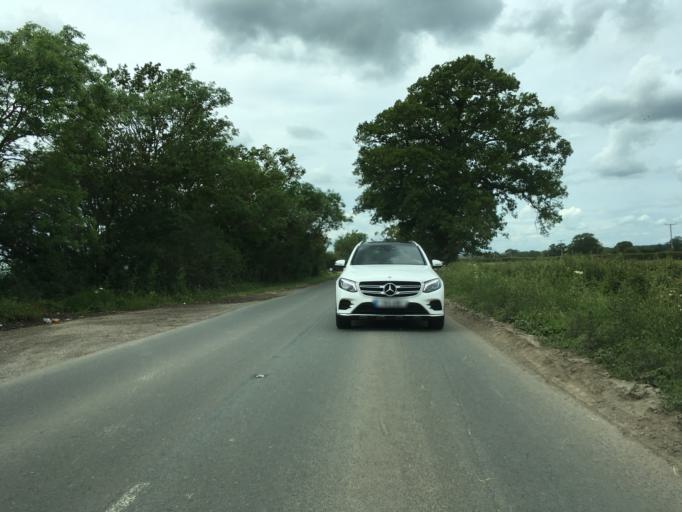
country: GB
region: England
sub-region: Wiltshire
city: Royal Wootton Bassett
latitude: 51.5601
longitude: -1.9237
